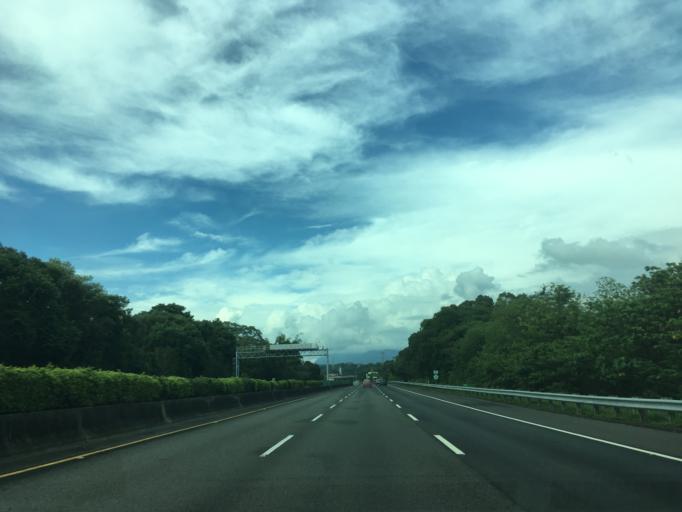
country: TW
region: Taiwan
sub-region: Chiayi
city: Jiayi Shi
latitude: 23.4574
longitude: 120.4903
